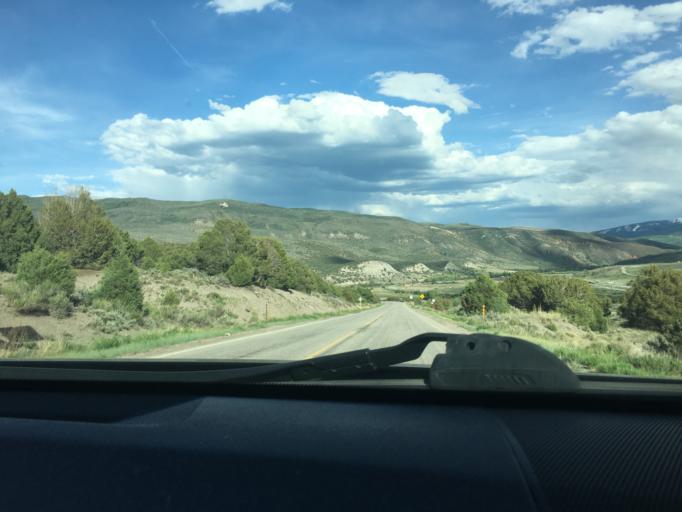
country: US
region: Colorado
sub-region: Eagle County
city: Edwards
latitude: 39.7056
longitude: -106.6840
